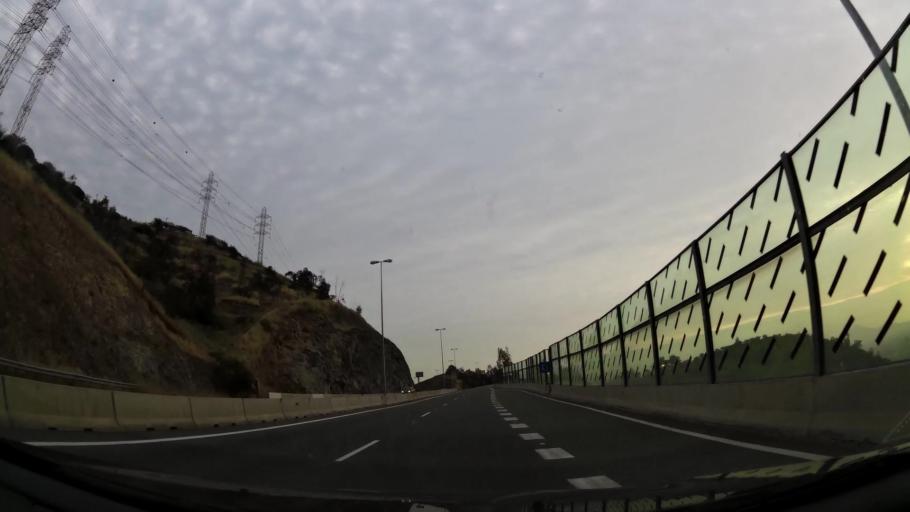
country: CL
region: Santiago Metropolitan
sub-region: Provincia de Santiago
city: Villa Presidente Frei, Nunoa, Santiago, Chile
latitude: -33.3801
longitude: -70.6036
